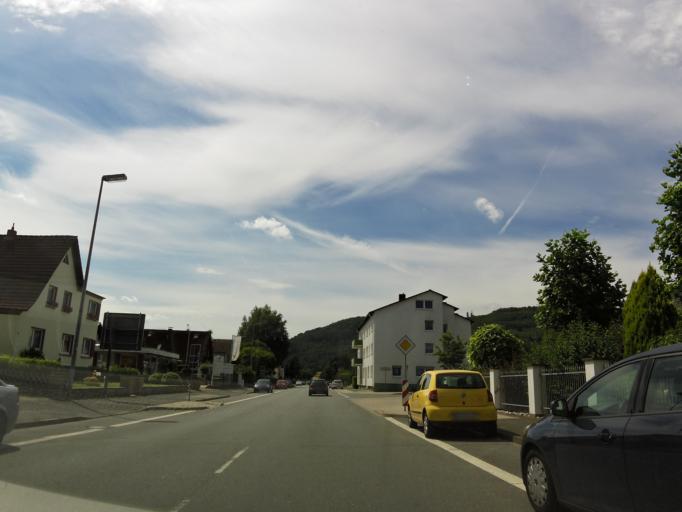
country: DE
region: North Rhine-Westphalia
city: Beverungen
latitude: 51.6608
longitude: 9.3721
